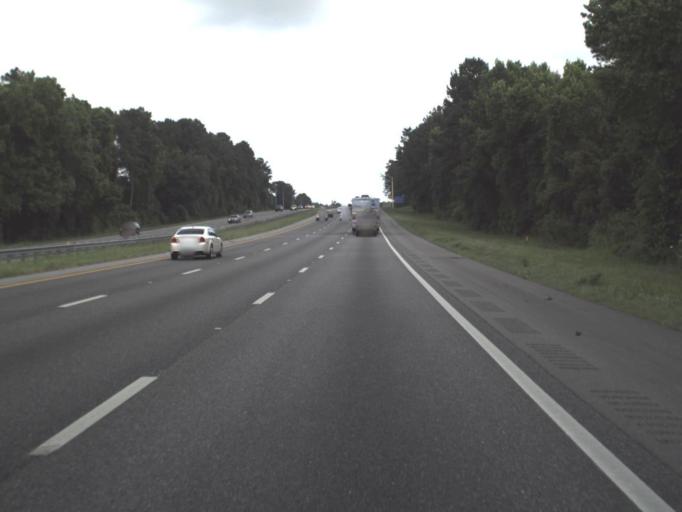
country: US
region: Florida
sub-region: Alachua County
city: High Springs
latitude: 29.9686
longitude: -82.5746
